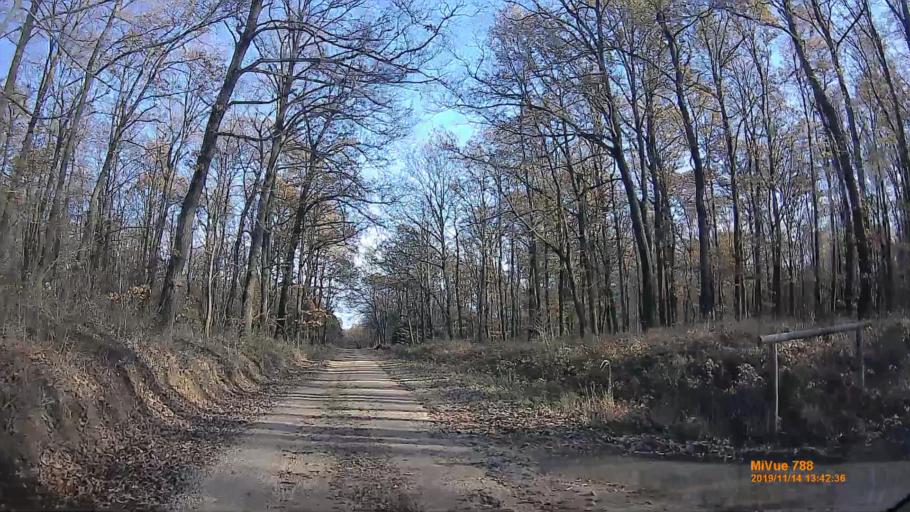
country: HU
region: Veszprem
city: Veszprem
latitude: 47.1827
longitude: 17.9219
